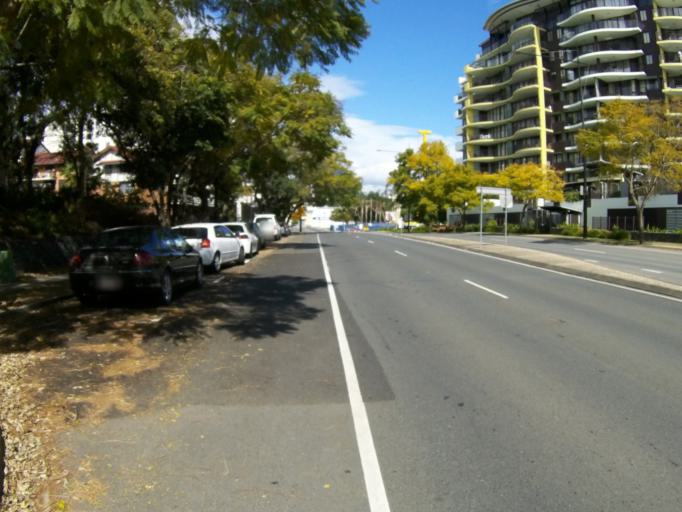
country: AU
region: Queensland
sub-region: Brisbane
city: Toowong
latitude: -27.4804
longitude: 152.9962
